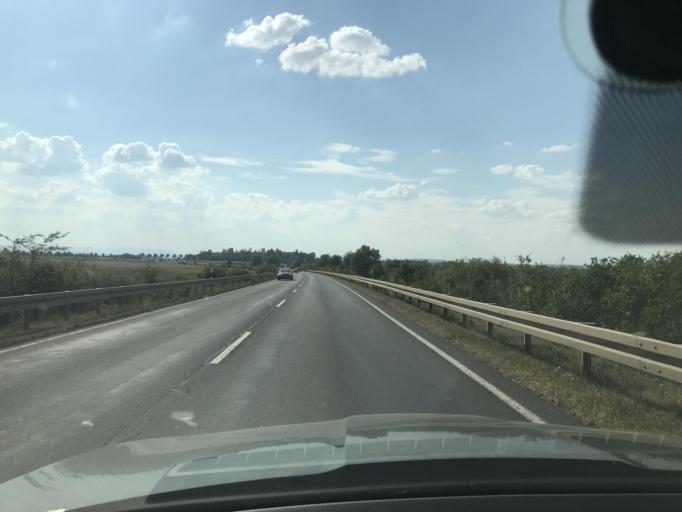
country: DE
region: Saxony-Anhalt
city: Groeningen
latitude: 51.9462
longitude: 11.2034
